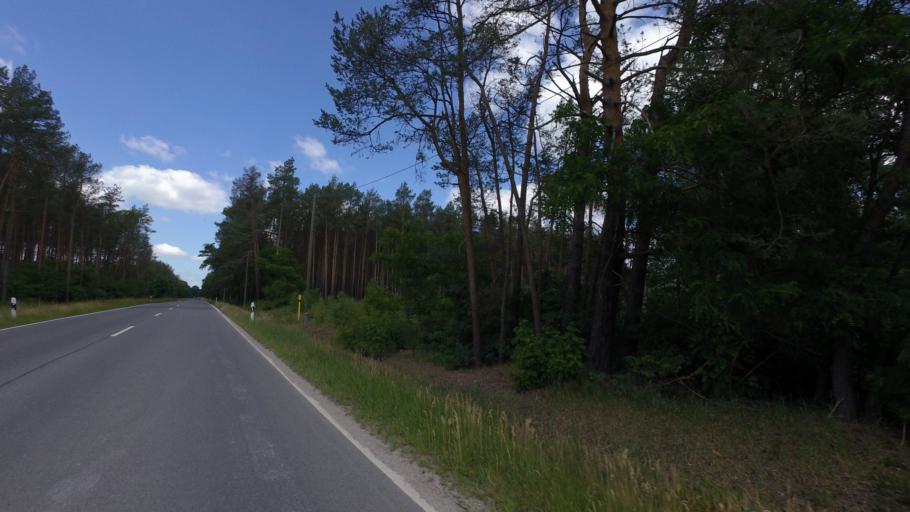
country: DE
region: Brandenburg
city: Finsterwalde
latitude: 51.6546
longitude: 13.6691
